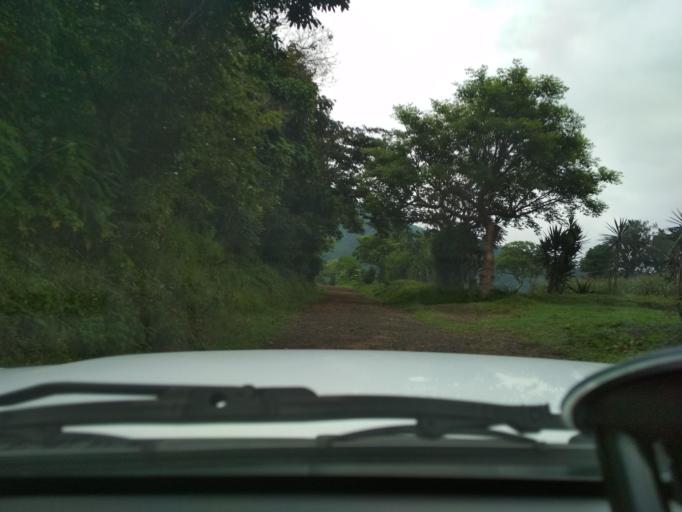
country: MX
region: Veracruz
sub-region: Ixtaczoquitlan
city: Buenavista
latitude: 18.9225
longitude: -97.0466
